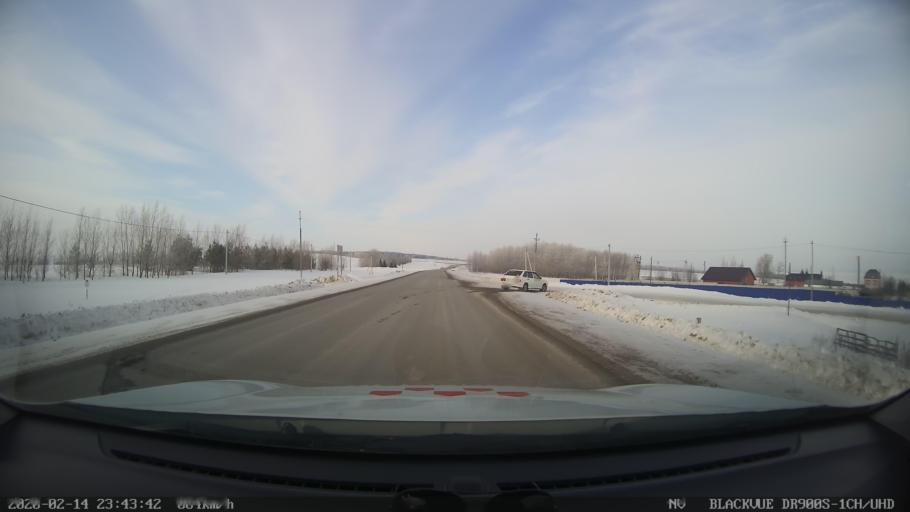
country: RU
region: Tatarstan
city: Kuybyshevskiy Zaton
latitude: 55.2050
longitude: 49.2487
